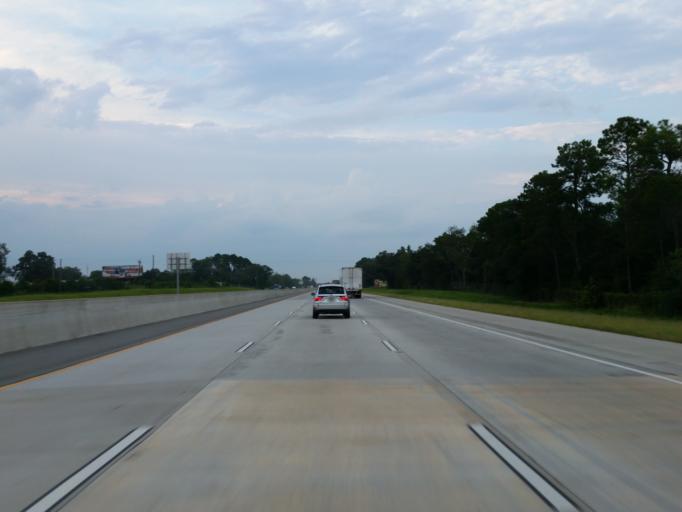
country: US
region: Georgia
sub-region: Cook County
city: Sparks
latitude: 31.2780
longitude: -83.4741
